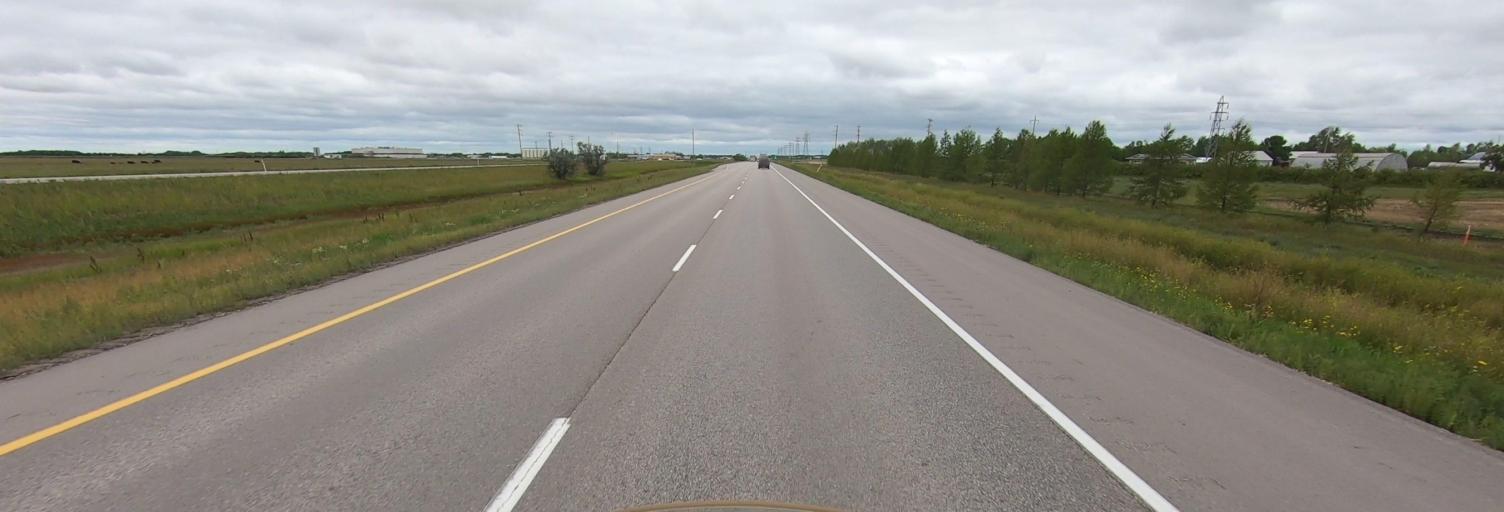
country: CA
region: Manitoba
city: Headingley
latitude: 49.8999
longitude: -97.7193
